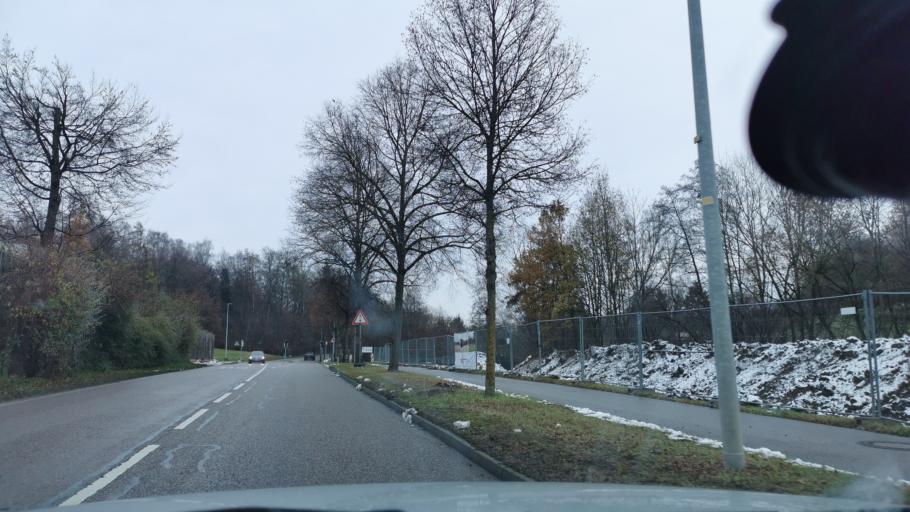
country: DE
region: Baden-Wuerttemberg
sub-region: Regierungsbezirk Stuttgart
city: Goeppingen
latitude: 48.7040
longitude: 9.6772
